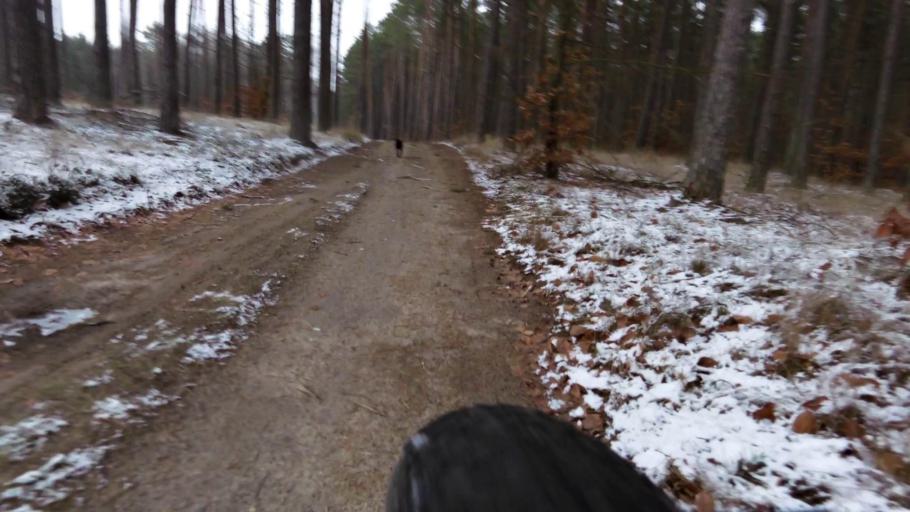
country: PL
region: West Pomeranian Voivodeship
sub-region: Powiat walecki
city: Miroslawiec
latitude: 53.2980
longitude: 16.0639
